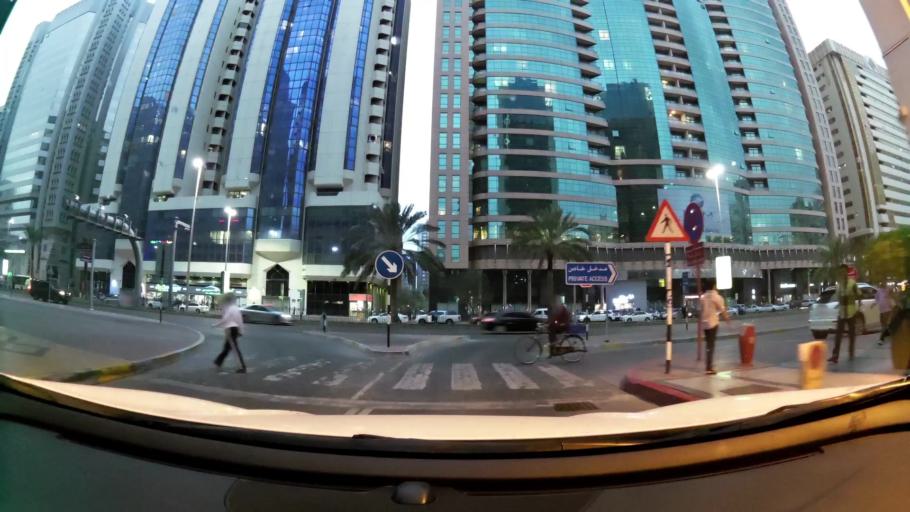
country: AE
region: Abu Dhabi
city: Abu Dhabi
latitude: 24.4911
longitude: 54.3656
